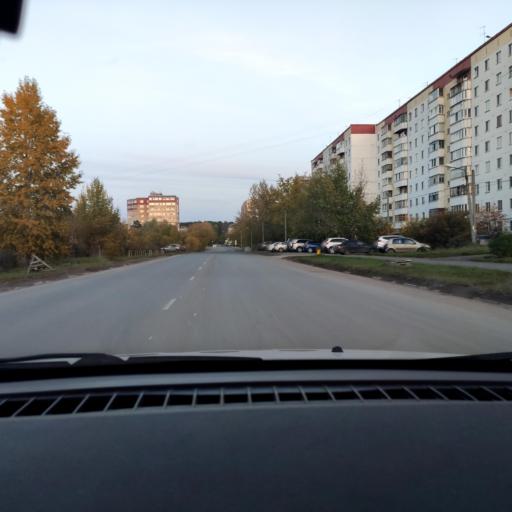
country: RU
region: Perm
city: Overyata
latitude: 58.0276
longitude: 55.8350
